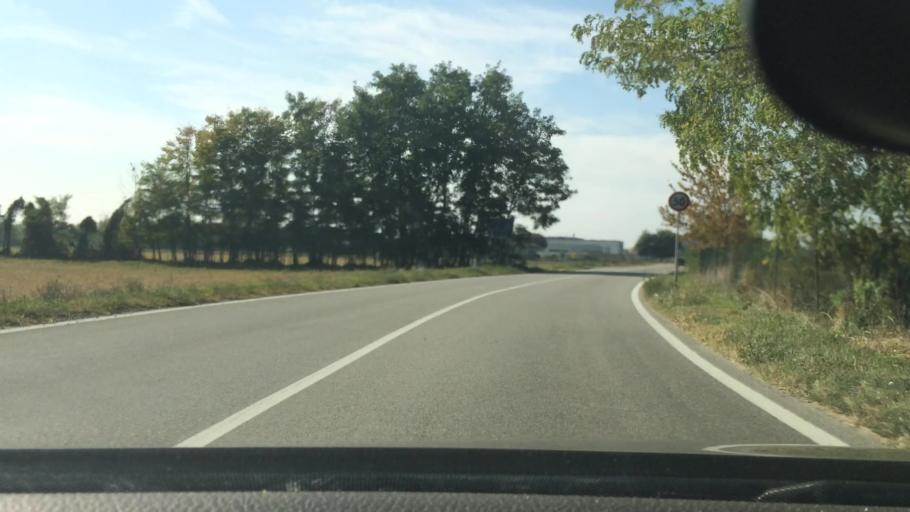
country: IT
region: Lombardy
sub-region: Citta metropolitana di Milano
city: Cerro Maggiore
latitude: 45.6042
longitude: 8.9703
